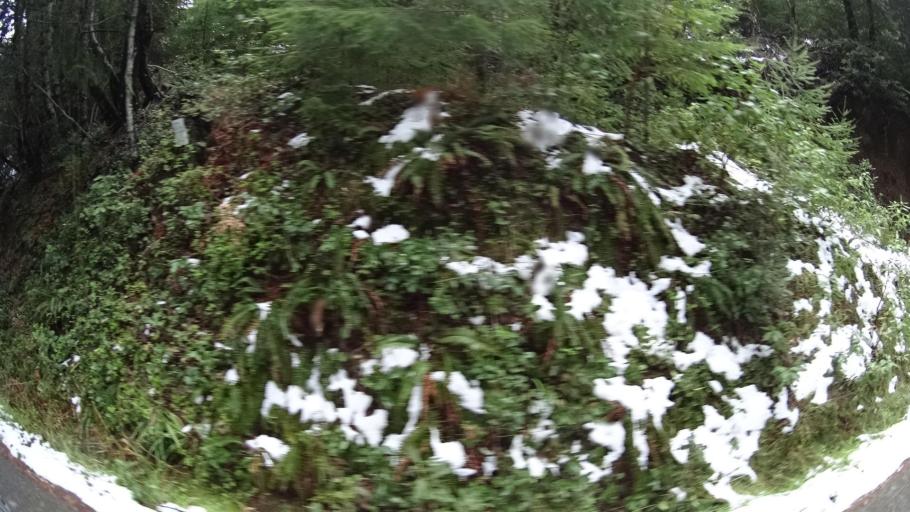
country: US
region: California
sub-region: Humboldt County
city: Blue Lake
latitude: 40.8805
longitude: -123.8802
